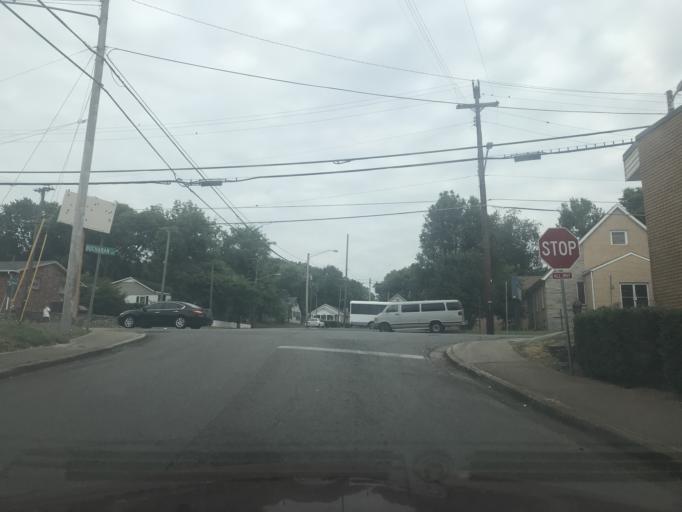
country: US
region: Tennessee
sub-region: Davidson County
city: Nashville
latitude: 36.1799
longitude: -86.8144
